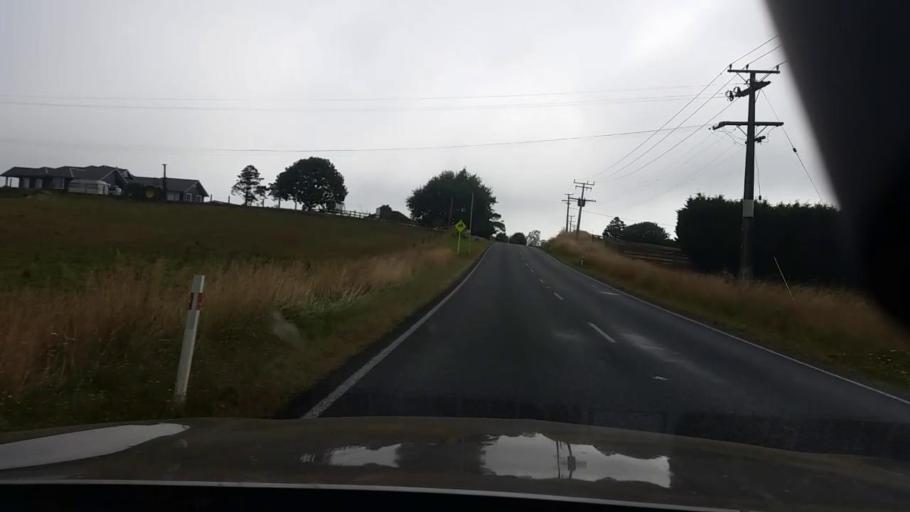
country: NZ
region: Waikato
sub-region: Hamilton City
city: Hamilton
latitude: -37.6217
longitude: 175.3312
